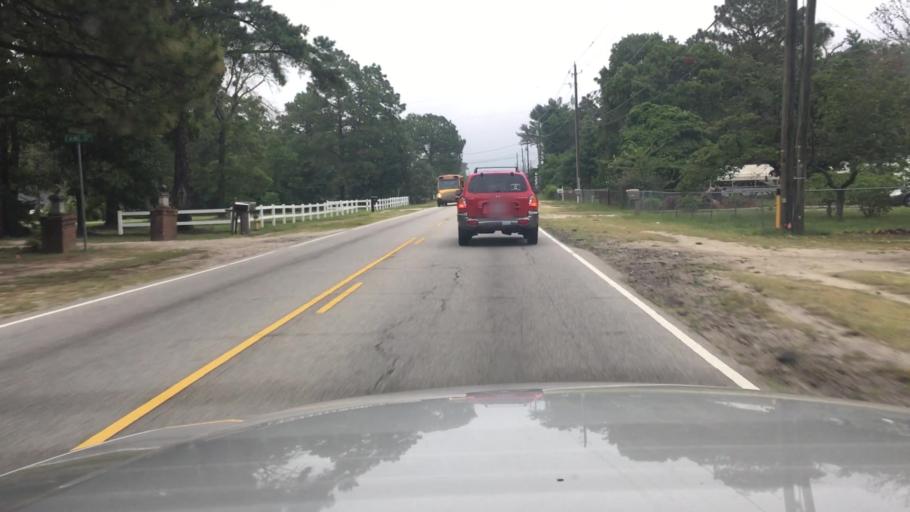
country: US
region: North Carolina
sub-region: Cumberland County
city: Hope Mills
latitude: 34.9785
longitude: -78.9826
